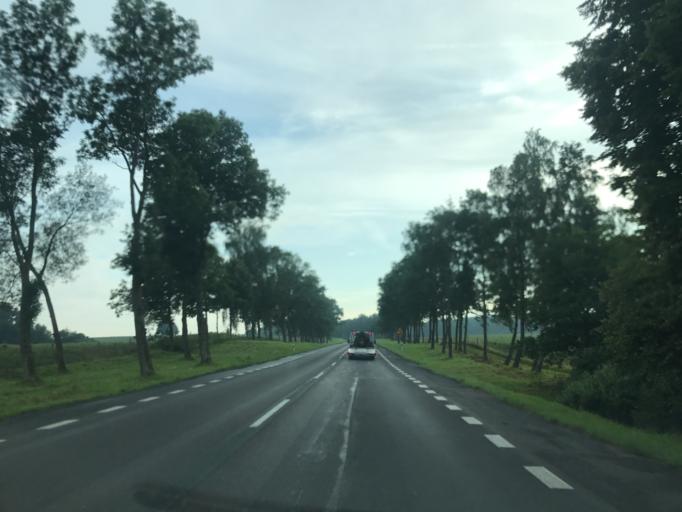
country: PL
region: West Pomeranian Voivodeship
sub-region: Powiat bialogardzki
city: Karlino
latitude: 54.0207
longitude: 15.8391
